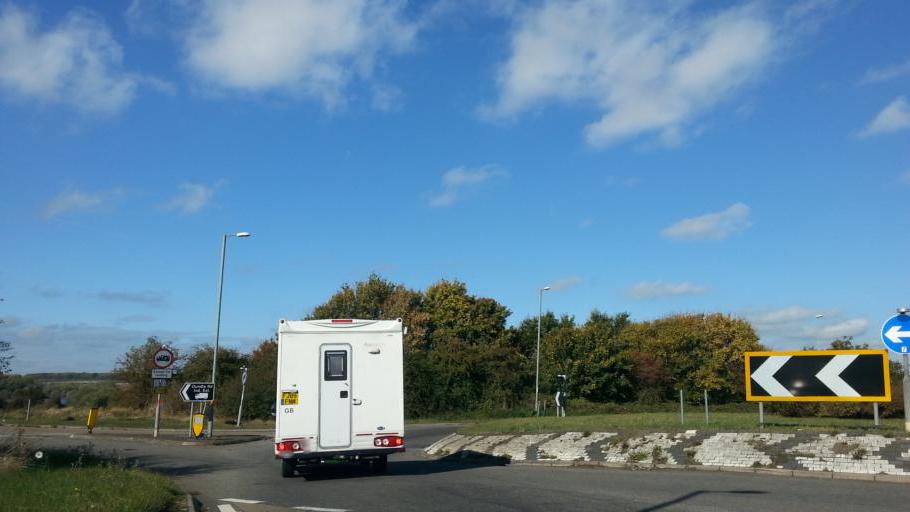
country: GB
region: England
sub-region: Northamptonshire
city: Thrapston
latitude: 52.4033
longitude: -0.5199
